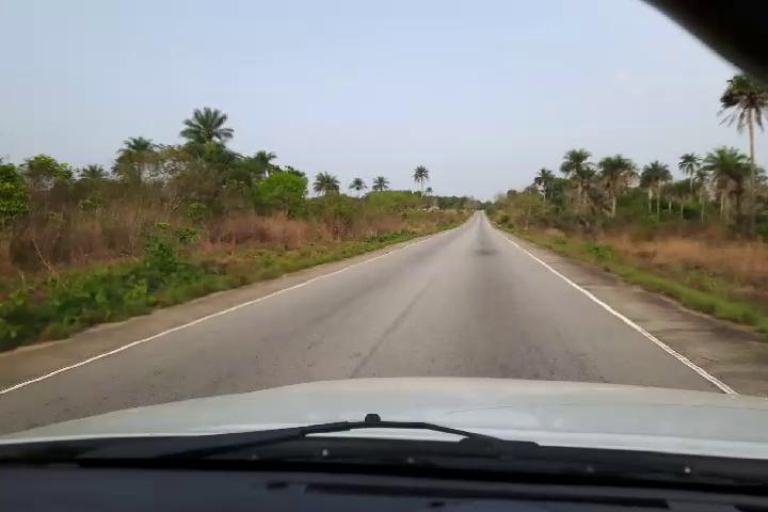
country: SL
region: Eastern Province
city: Blama
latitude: 7.9395
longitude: -11.4967
